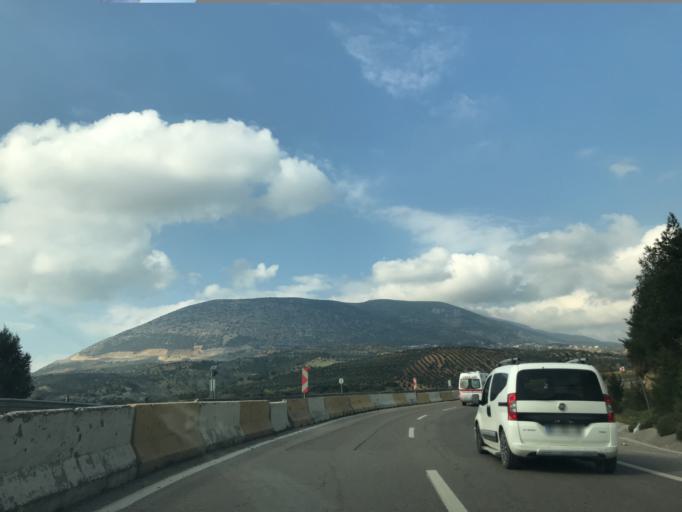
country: TR
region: Hatay
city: Belen
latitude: 36.4577
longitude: 36.2709
